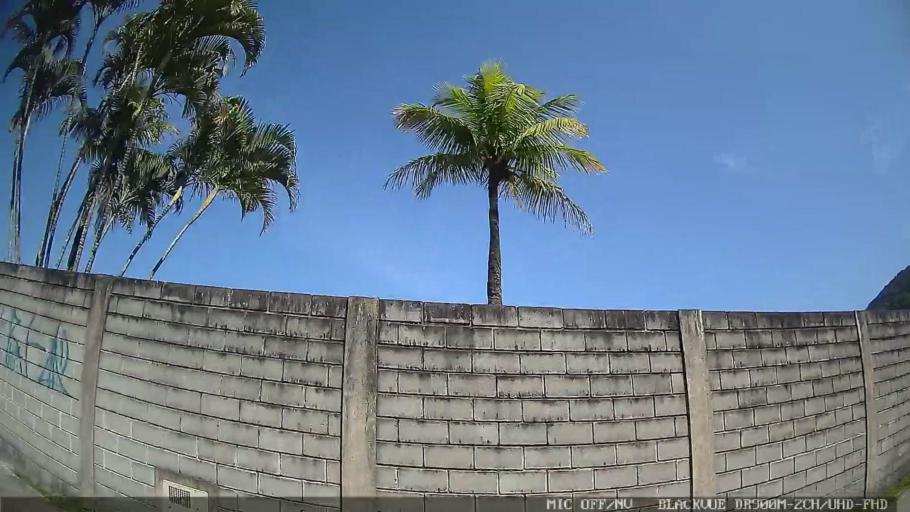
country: BR
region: Sao Paulo
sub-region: Guaruja
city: Guaruja
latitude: -24.0156
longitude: -46.2904
